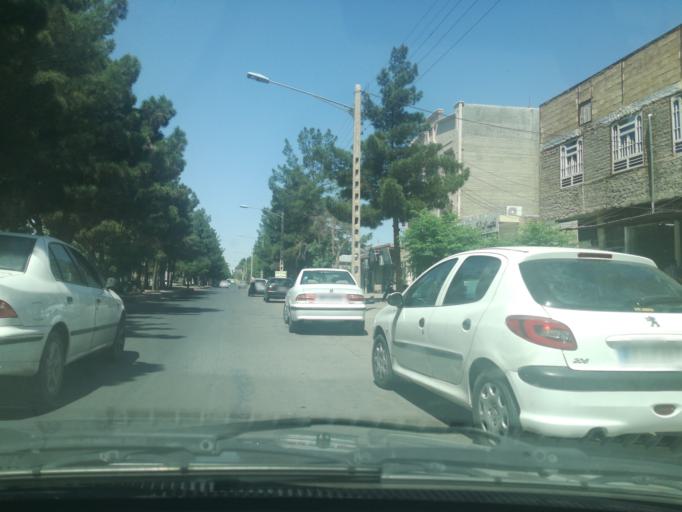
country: IR
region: Razavi Khorasan
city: Sarakhs
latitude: 36.5373
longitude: 61.1585
